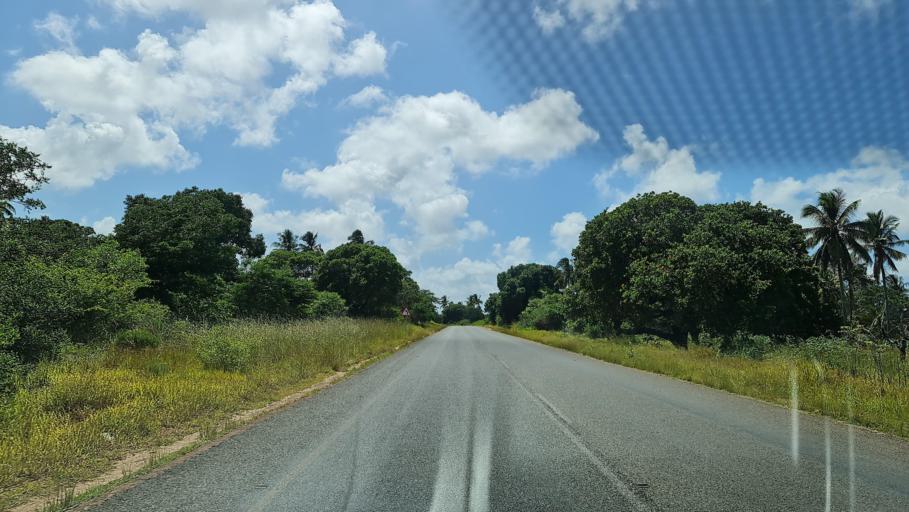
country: MZ
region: Inhambane
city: Maxixe
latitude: -24.5401
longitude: 34.9303
